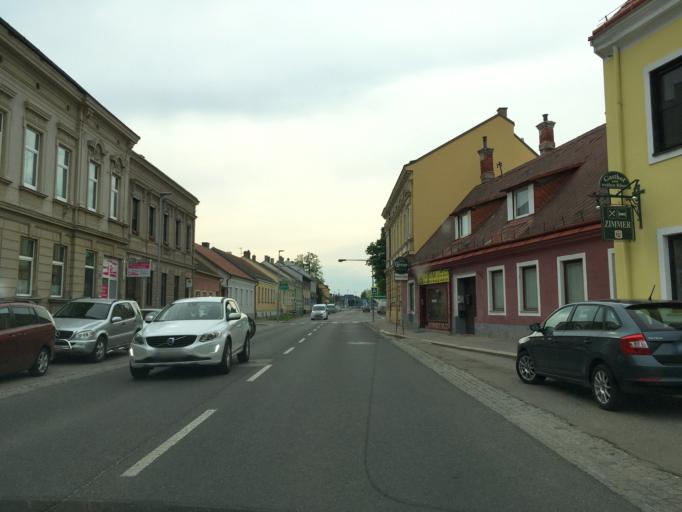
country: AT
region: Lower Austria
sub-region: Politischer Bezirk Korneuburg
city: Stockerau
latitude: 48.3851
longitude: 16.2022
